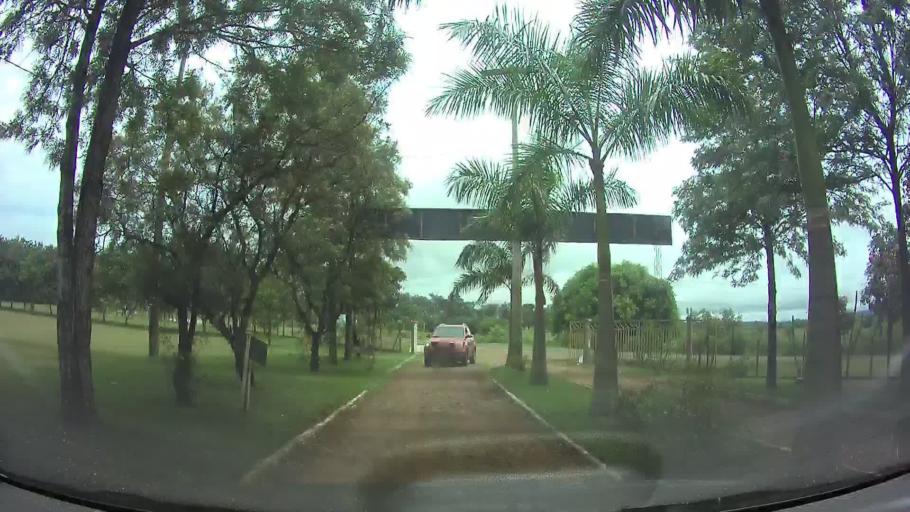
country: PY
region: Paraguari
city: Ybycui
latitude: -25.9965
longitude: -57.0507
